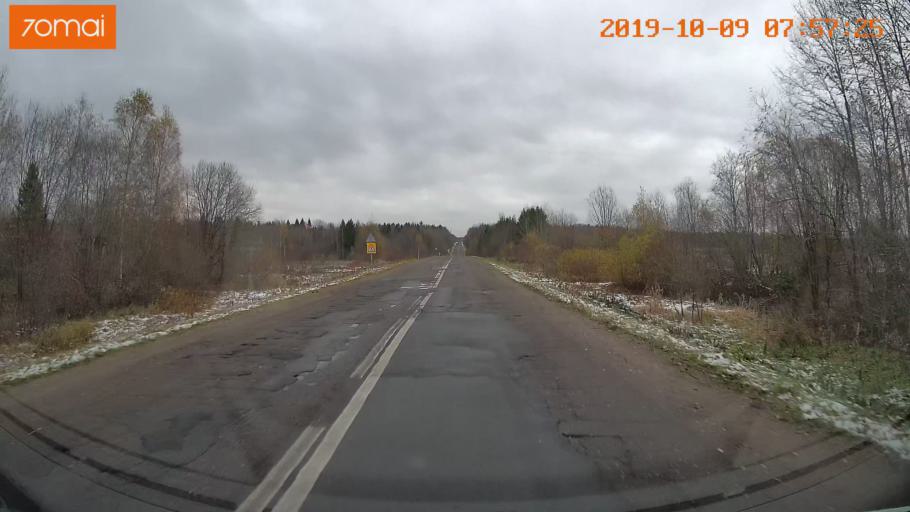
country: RU
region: Jaroslavl
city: Kukoboy
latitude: 58.6970
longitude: 39.9503
